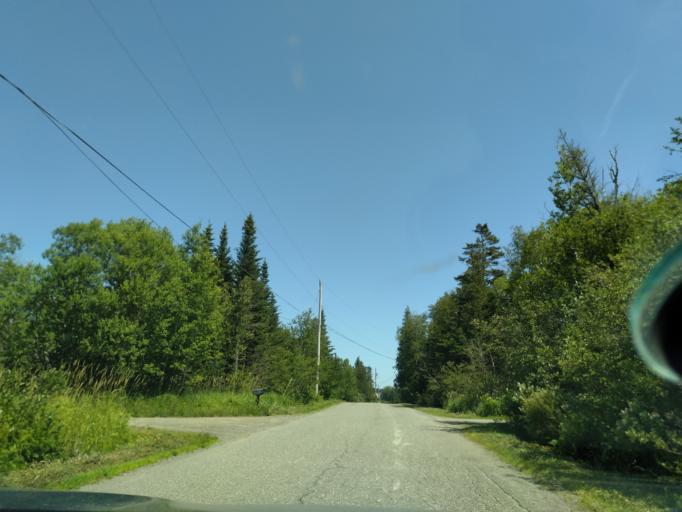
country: US
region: Maine
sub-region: Washington County
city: Eastport
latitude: 44.8320
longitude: -66.9951
